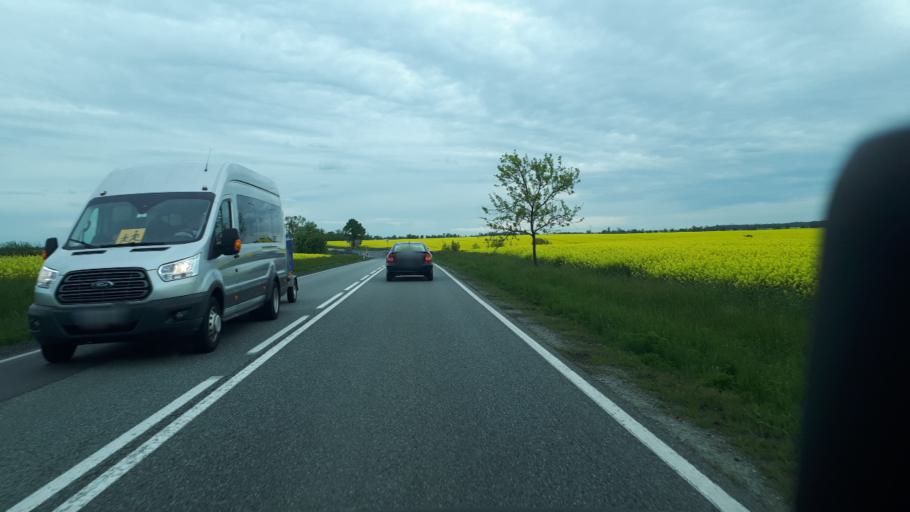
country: PL
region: Opole Voivodeship
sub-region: Powiat kluczborski
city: Byczyna
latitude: 51.0526
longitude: 18.1969
